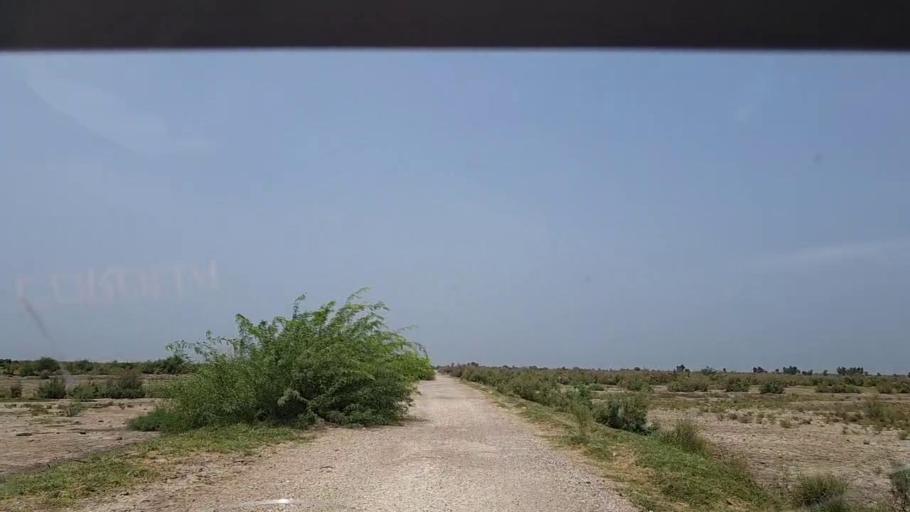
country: PK
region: Sindh
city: Adilpur
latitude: 27.8884
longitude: 69.2549
